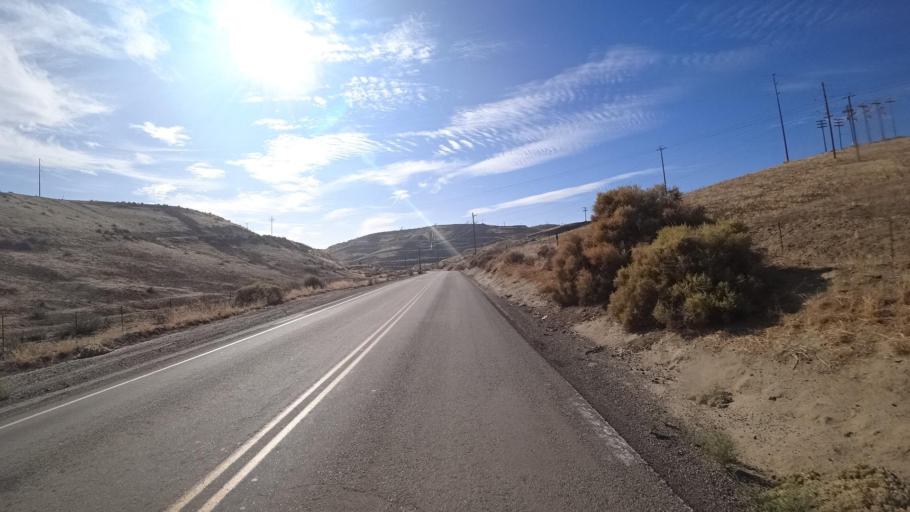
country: US
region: California
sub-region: Kern County
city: Oildale
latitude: 35.5919
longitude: -118.9576
